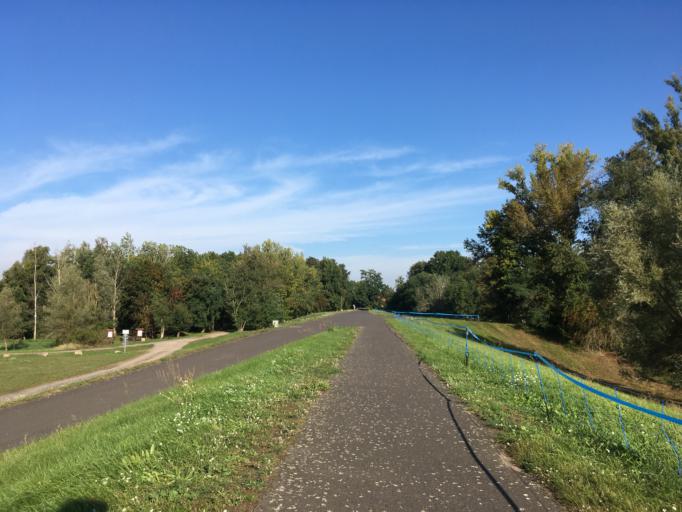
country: PL
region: Lubusz
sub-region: Powiat gorzowski
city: Kostrzyn nad Odra
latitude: 52.5692
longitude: 14.6212
